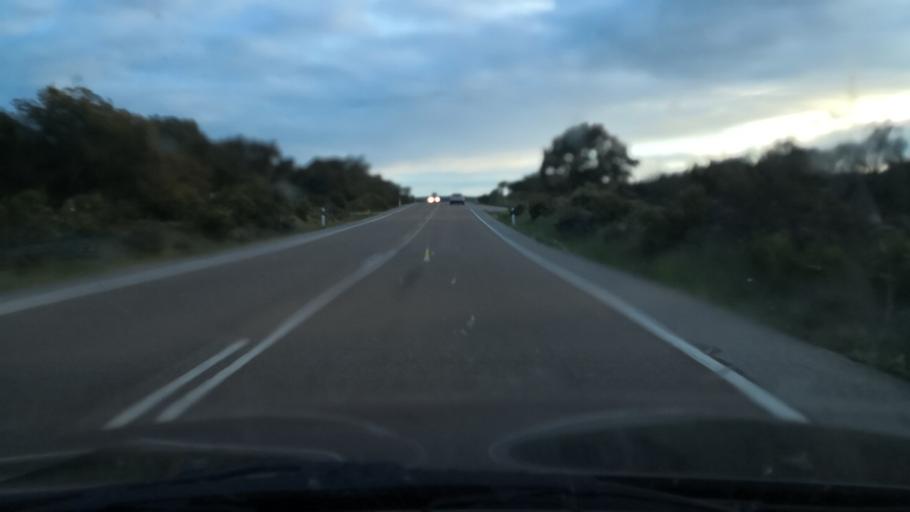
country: ES
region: Extremadura
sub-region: Provincia de Badajoz
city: Puebla de Obando
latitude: 39.2219
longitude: -6.5762
